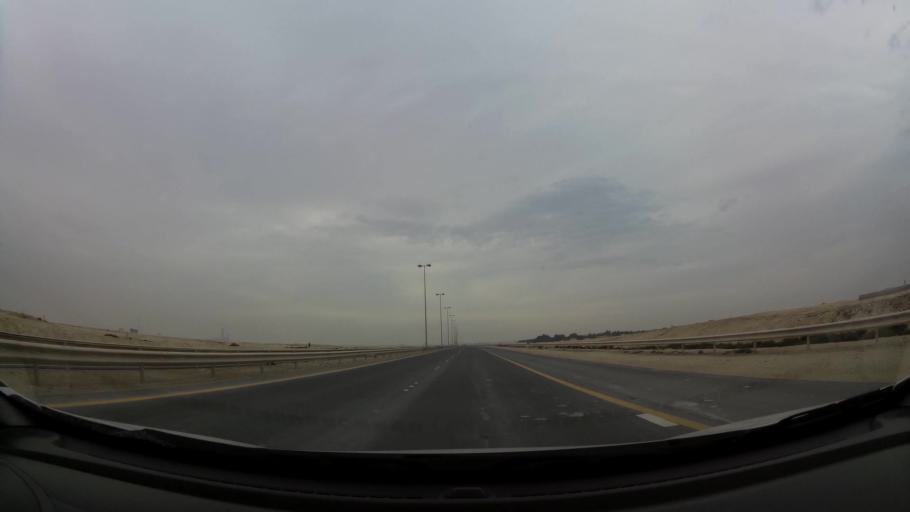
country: BH
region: Central Governorate
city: Dar Kulayb
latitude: 26.0098
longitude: 50.6062
